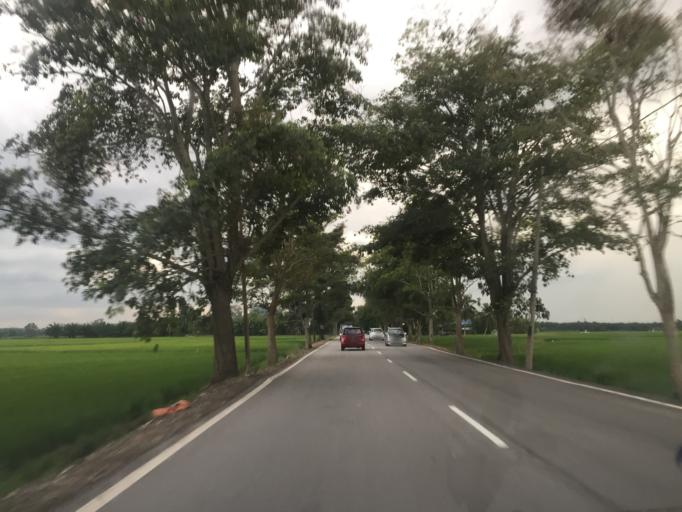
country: MY
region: Penang
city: Tasek Glugor
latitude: 5.5452
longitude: 100.5066
